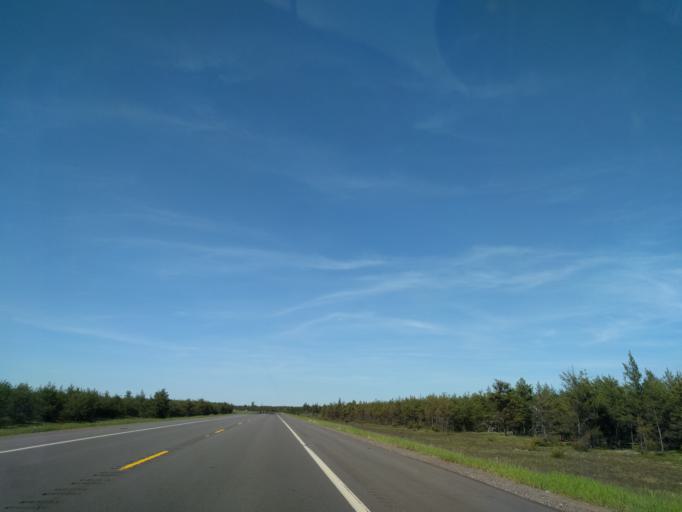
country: US
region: Michigan
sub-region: Marquette County
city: K. I. Sawyer Air Force Base
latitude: 46.3506
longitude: -87.4117
